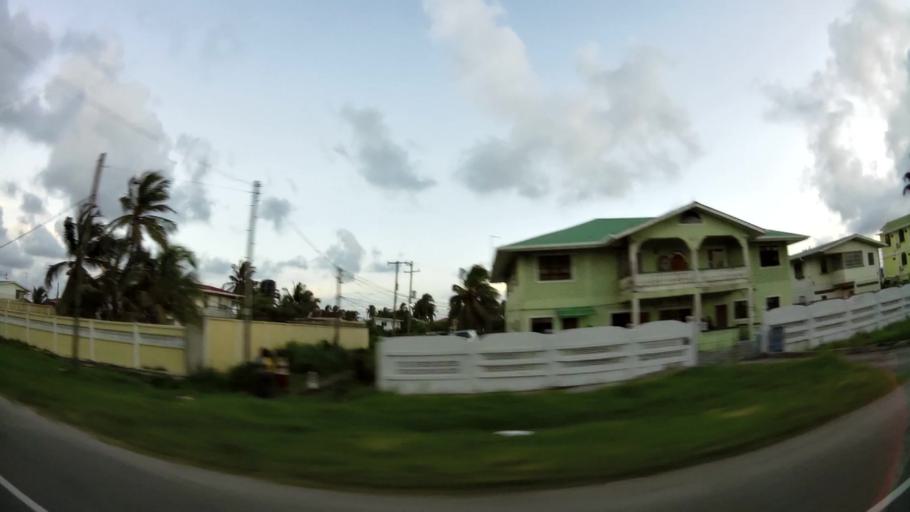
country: GY
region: Demerara-Mahaica
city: Georgetown
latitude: 6.8260
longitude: -58.1211
